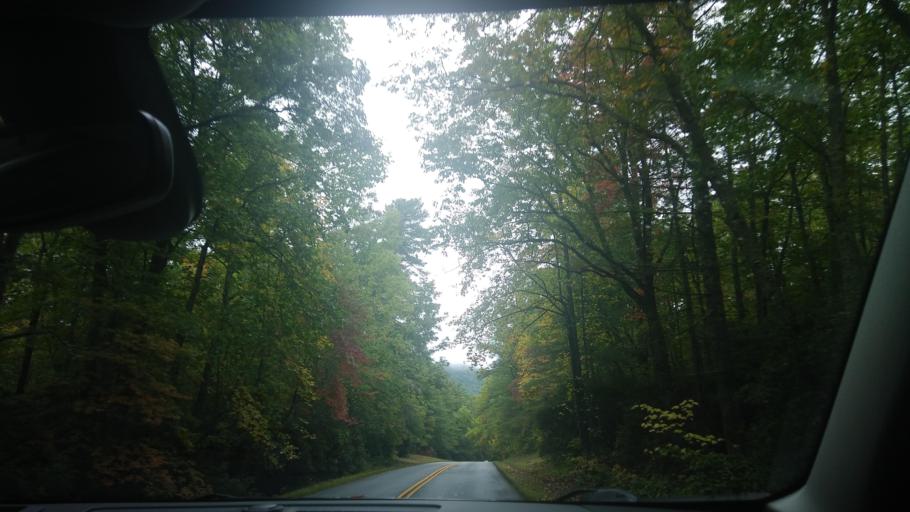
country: US
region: North Carolina
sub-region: Mitchell County
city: Spruce Pine
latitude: 35.8931
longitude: -81.9803
